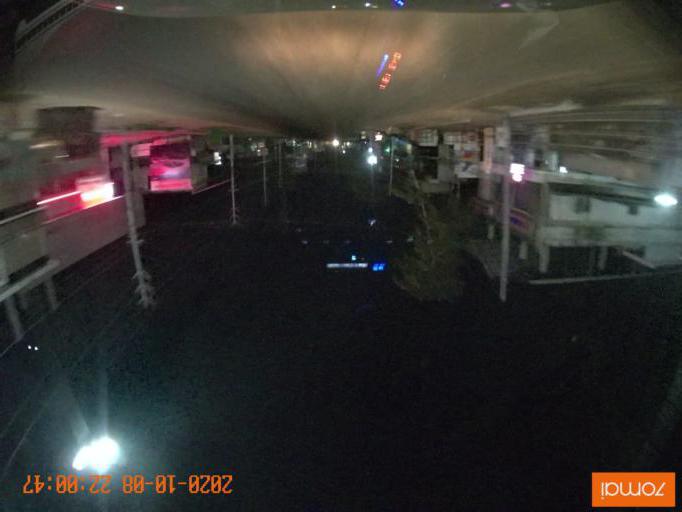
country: IN
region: Kerala
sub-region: Malappuram
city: Tirur
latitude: 10.9357
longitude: 75.9074
